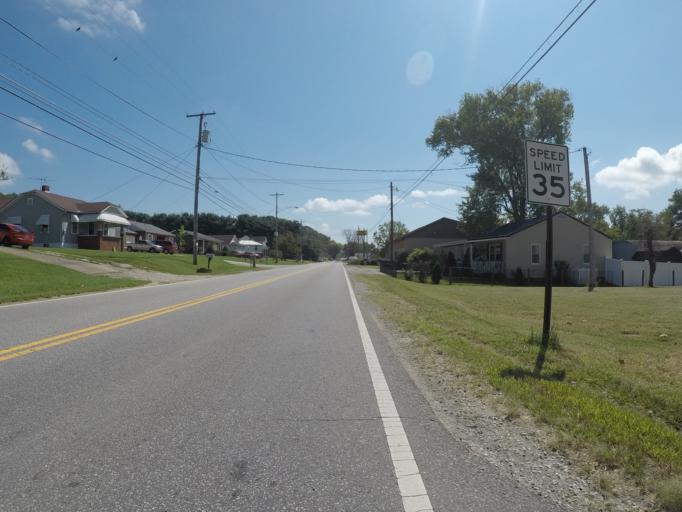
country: US
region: Ohio
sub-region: Lawrence County
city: South Point
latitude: 38.4113
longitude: -82.5775
